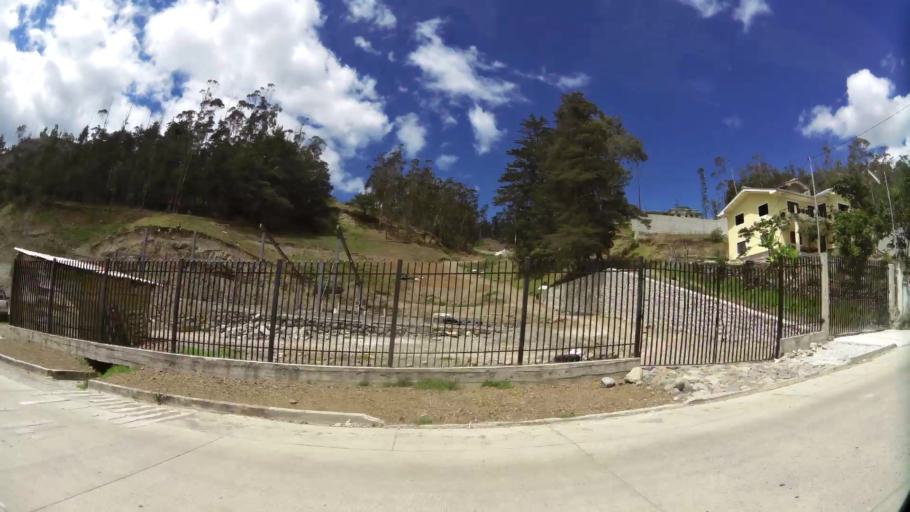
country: EC
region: Azuay
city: Cuenca
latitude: -3.1513
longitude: -79.1466
